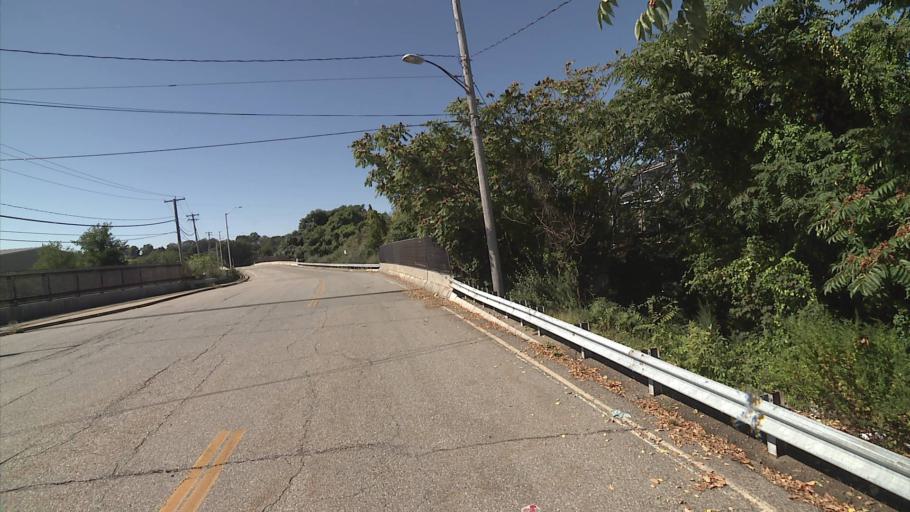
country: US
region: Connecticut
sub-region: New London County
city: New London
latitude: 41.3623
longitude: -72.0920
